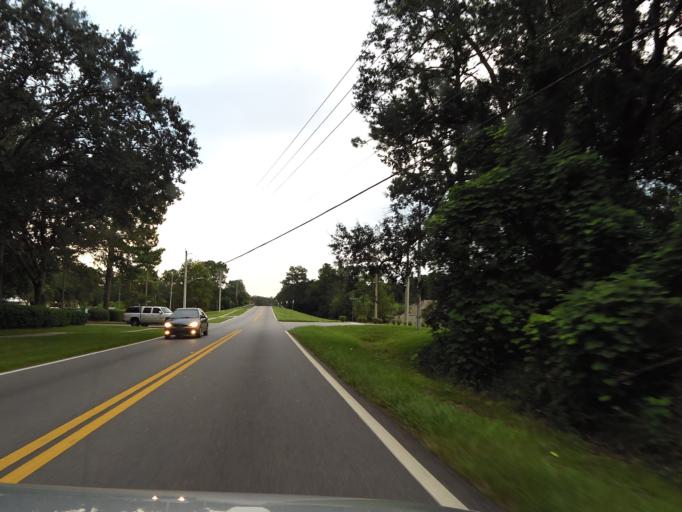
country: US
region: Florida
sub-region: Clay County
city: Bellair-Meadowbrook Terrace
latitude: 30.2844
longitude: -81.7746
